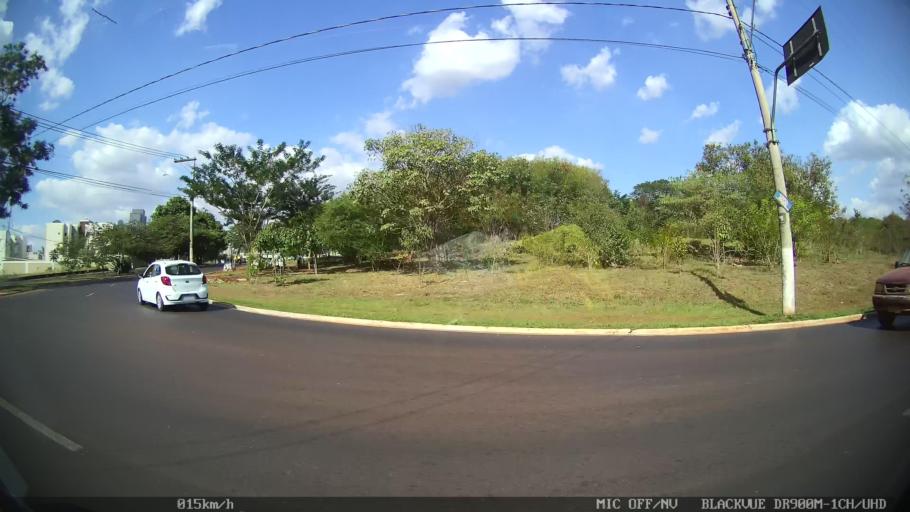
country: BR
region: Sao Paulo
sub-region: Ribeirao Preto
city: Ribeirao Preto
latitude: -21.2041
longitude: -47.8270
